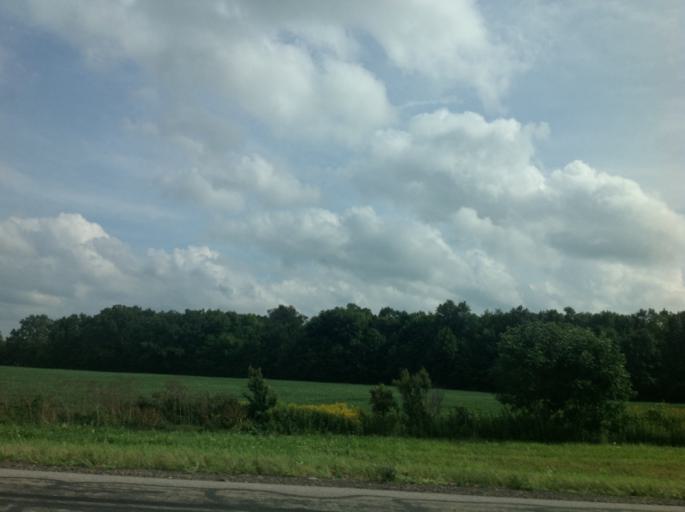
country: US
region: Ohio
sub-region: Ashland County
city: Ashland
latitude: 40.8257
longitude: -82.3274
